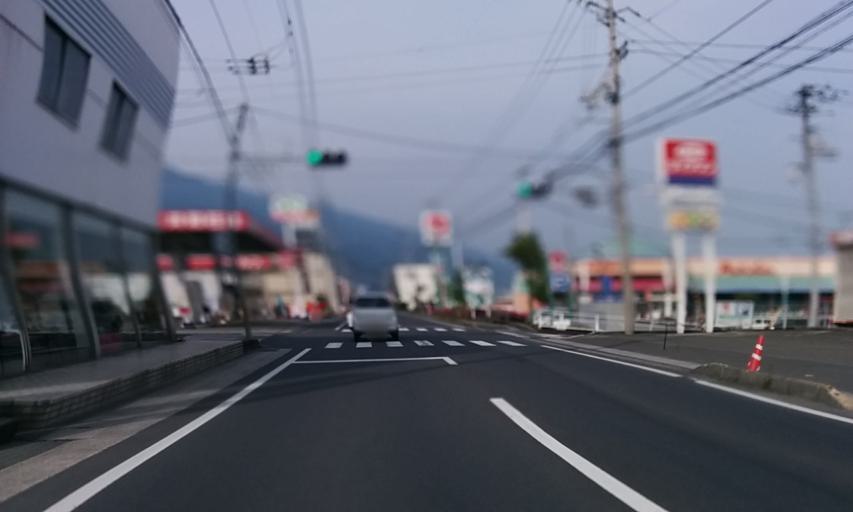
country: JP
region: Ehime
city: Kawanoecho
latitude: 33.9726
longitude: 133.5267
